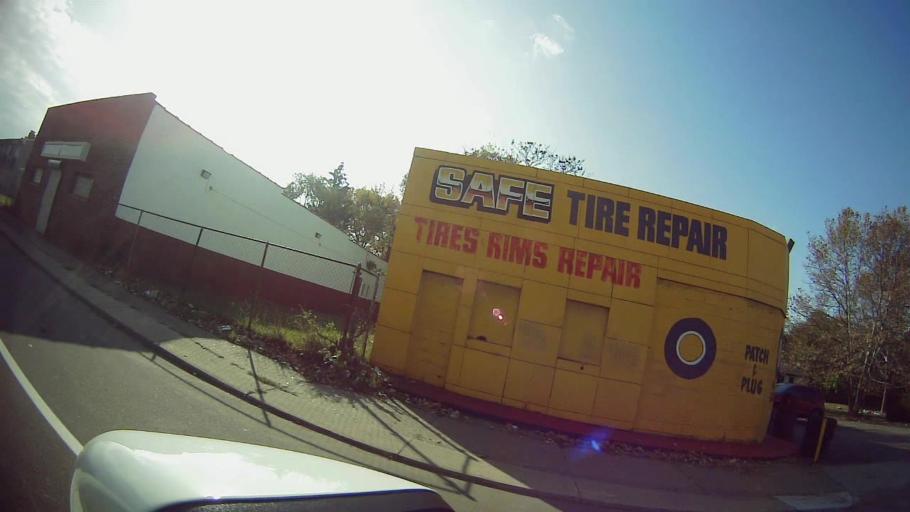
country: US
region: Michigan
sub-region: Oakland County
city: Hazel Park
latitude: 42.4421
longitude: -83.0803
